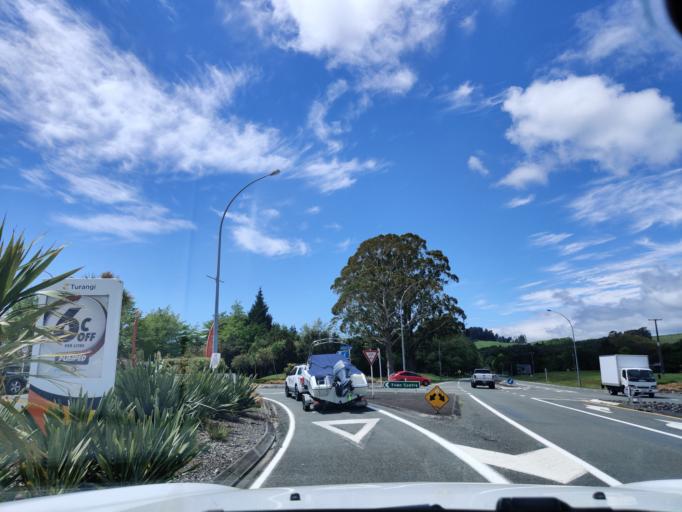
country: NZ
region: Waikato
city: Turangi
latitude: -38.9907
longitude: 175.8104
